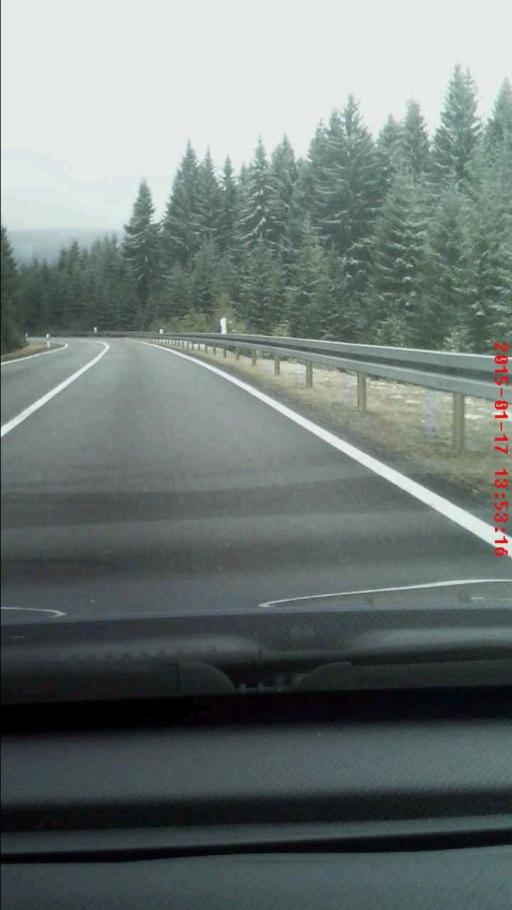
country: DE
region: Thuringia
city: Goldisthal
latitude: 50.4986
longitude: 11.0359
